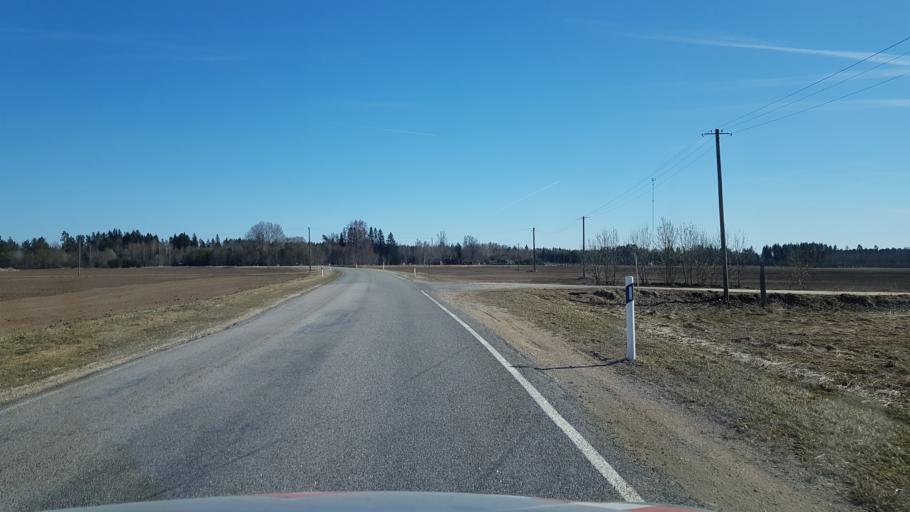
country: EE
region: Laeaene-Virumaa
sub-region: Vinni vald
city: Vinni
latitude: 59.2361
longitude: 26.6949
